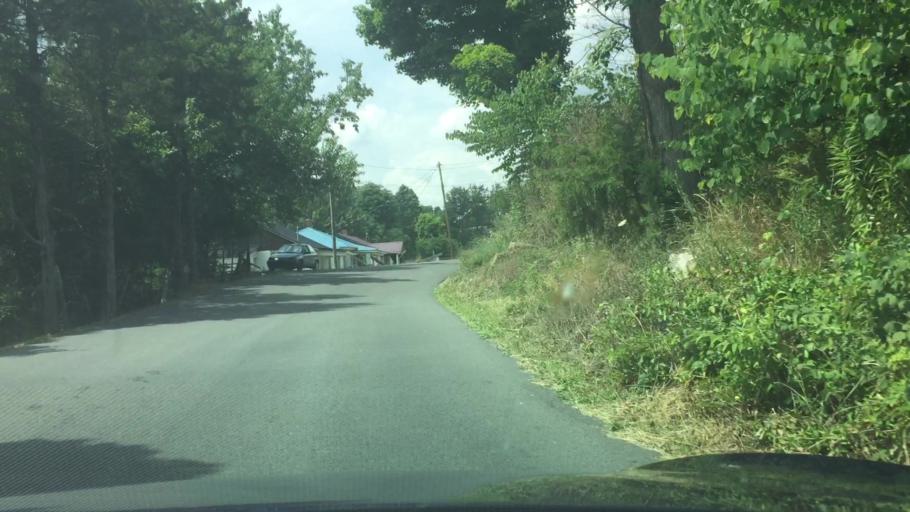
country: US
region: Virginia
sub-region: Wythe County
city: Wytheville
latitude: 36.9397
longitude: -81.0788
